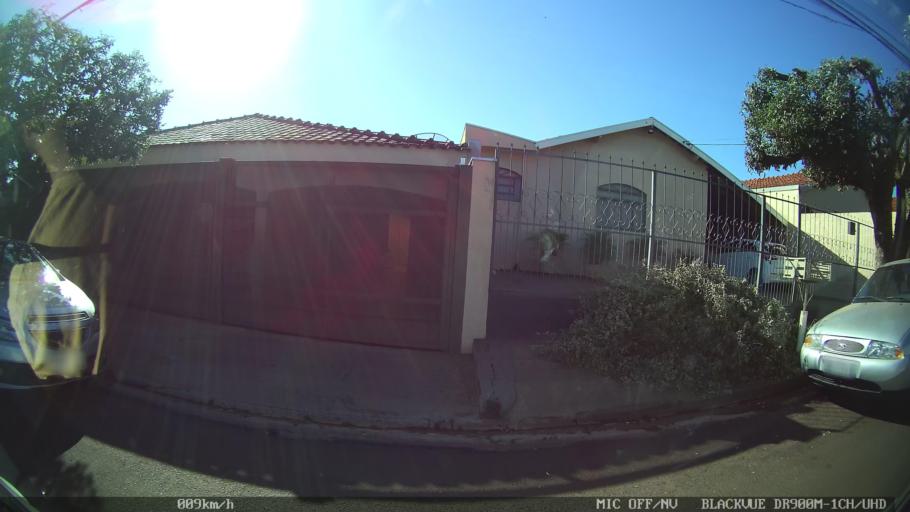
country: BR
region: Sao Paulo
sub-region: Olimpia
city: Olimpia
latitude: -20.7404
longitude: -48.9010
